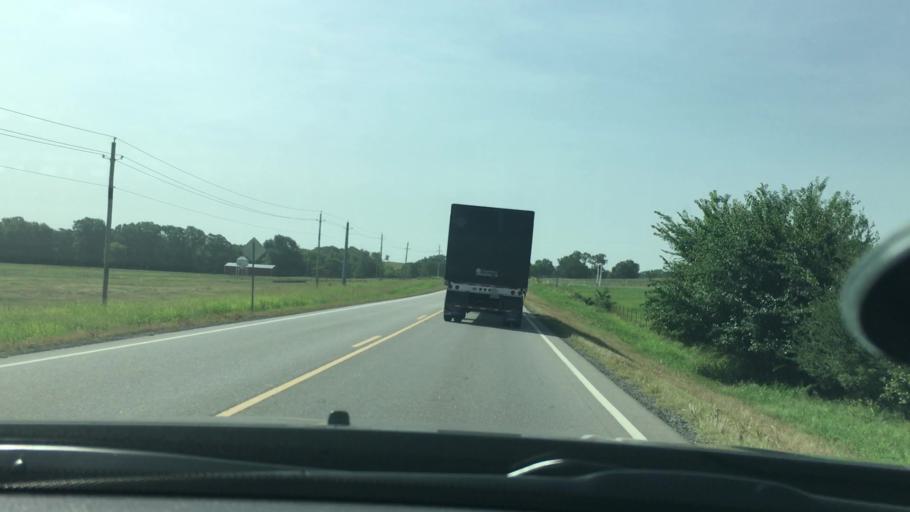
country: US
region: Oklahoma
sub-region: Atoka County
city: Atoka
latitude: 34.4094
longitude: -96.1821
